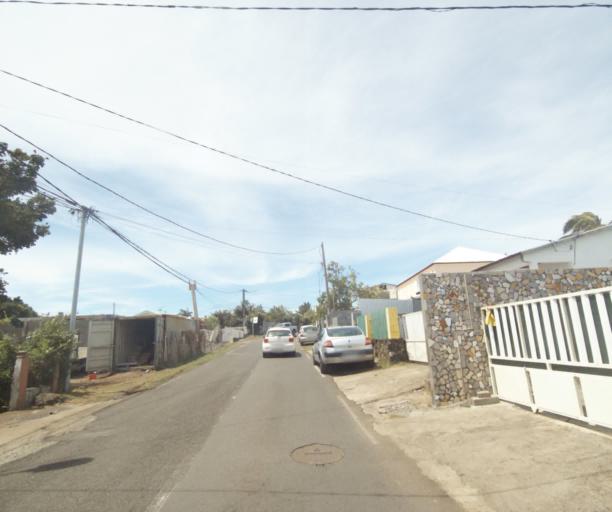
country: RE
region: Reunion
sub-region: Reunion
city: Saint-Paul
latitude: -21.0448
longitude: 55.2806
